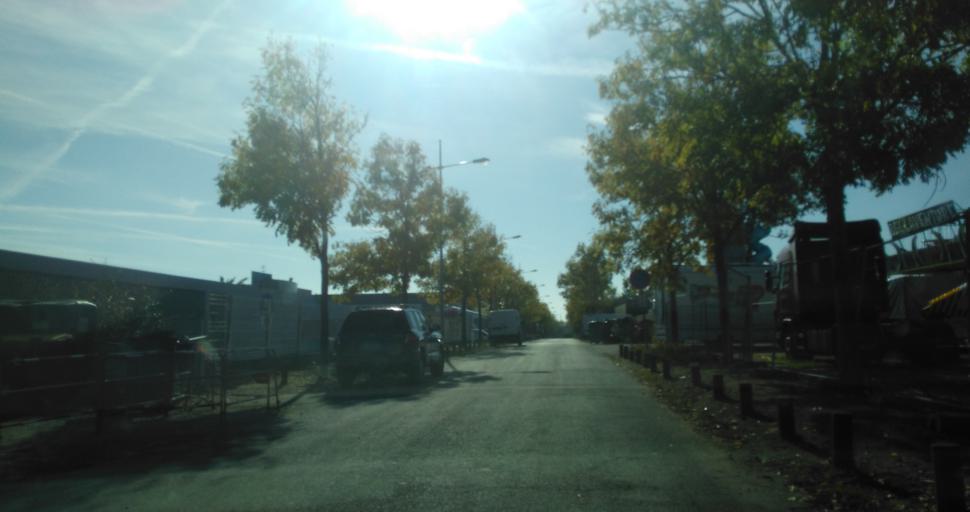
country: FR
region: Brittany
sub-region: Departement du Morbihan
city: Sene
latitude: 47.6368
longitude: -2.7636
